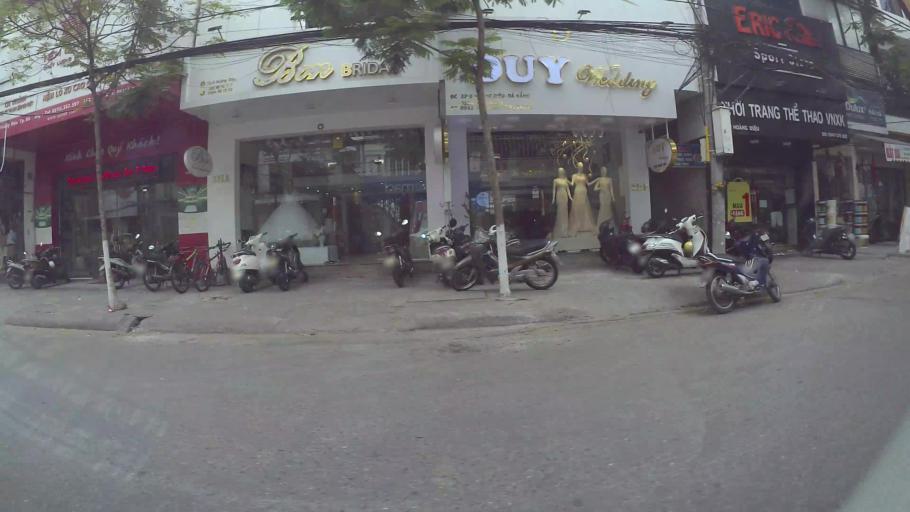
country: VN
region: Da Nang
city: Da Nang
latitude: 16.0561
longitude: 108.2173
